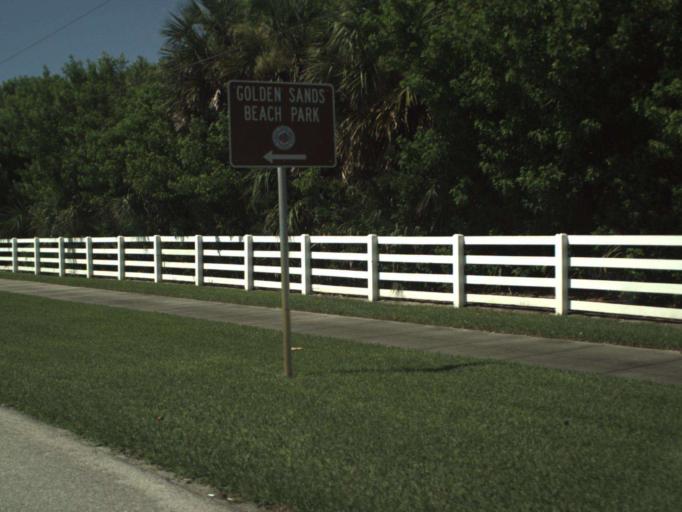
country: US
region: Florida
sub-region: Indian River County
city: Wabasso Beach
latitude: 27.7827
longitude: -80.4083
